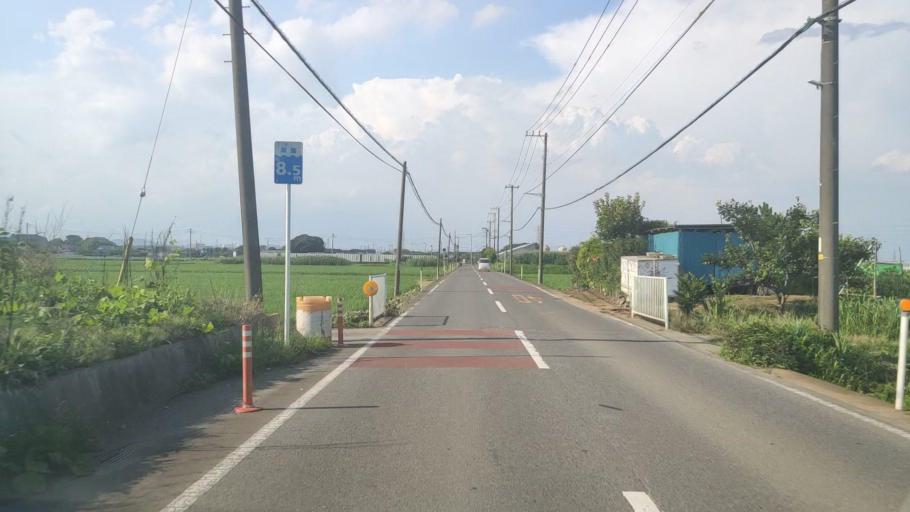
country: JP
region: Kanagawa
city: Isehara
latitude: 35.3657
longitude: 139.3281
